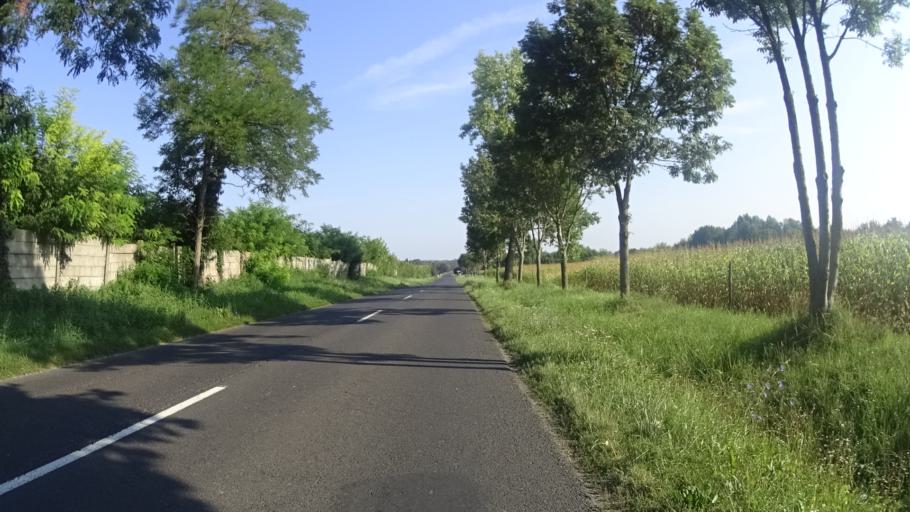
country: HU
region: Zala
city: Sarmellek
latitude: 46.6932
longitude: 17.1678
